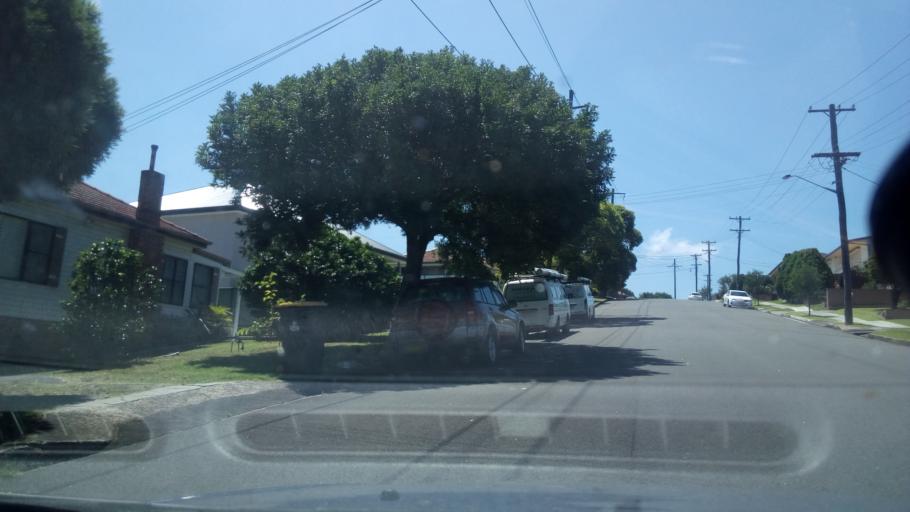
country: AU
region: New South Wales
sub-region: Wollongong
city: West Wollongong
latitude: -34.4259
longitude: 150.8667
